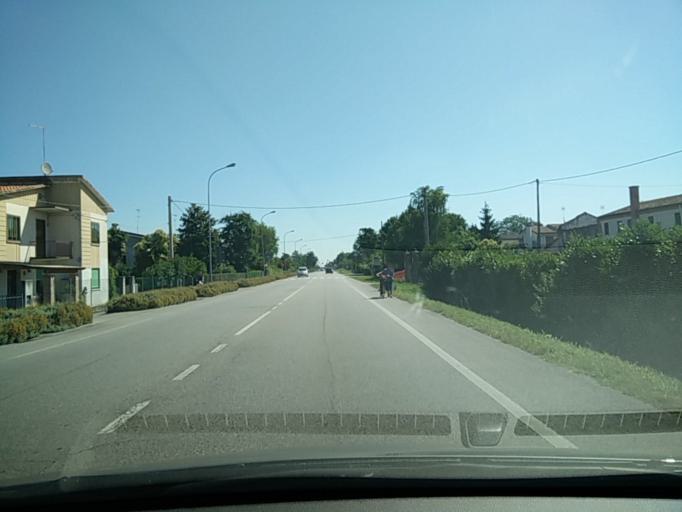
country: IT
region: Veneto
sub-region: Provincia di Venezia
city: San Dona di Piave
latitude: 45.6352
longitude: 12.6023
